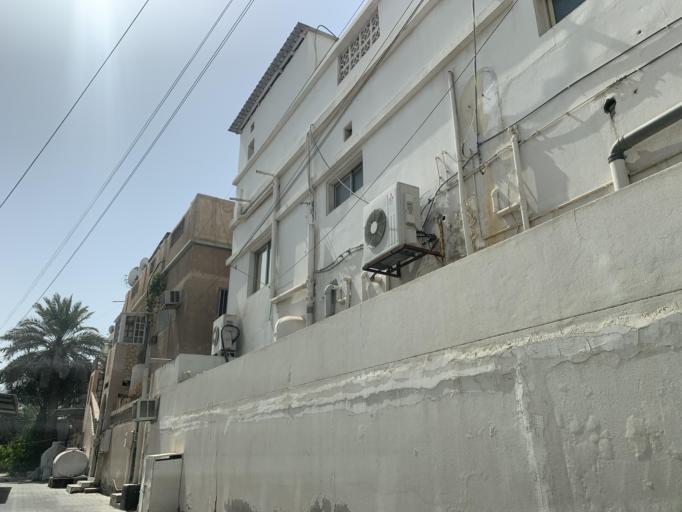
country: BH
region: Manama
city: Jidd Hafs
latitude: 26.2170
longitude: 50.5175
